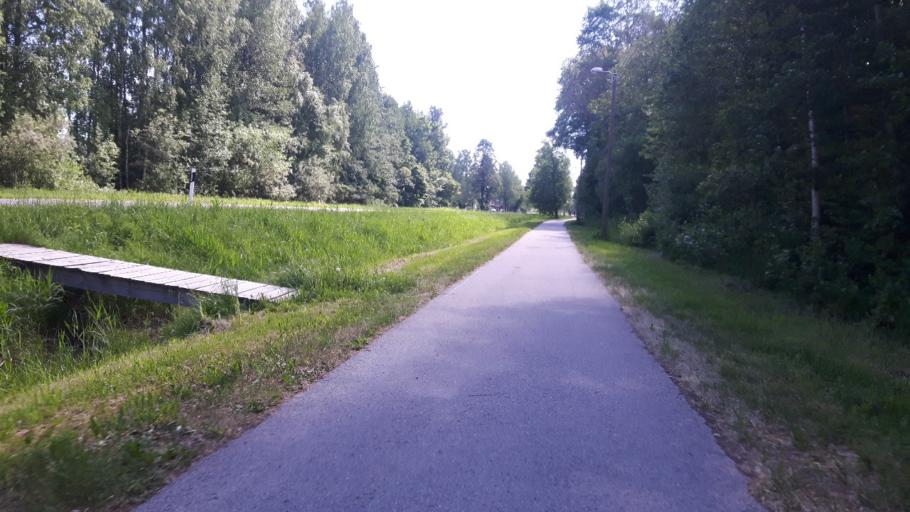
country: EE
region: Paernumaa
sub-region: Paikuse vald
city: Paikuse
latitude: 58.3837
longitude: 24.6360
